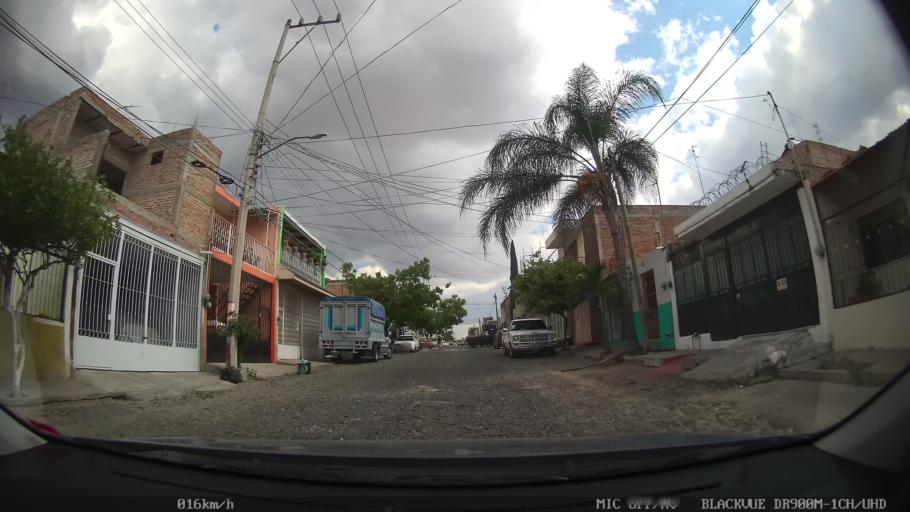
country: MX
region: Jalisco
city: Tlaquepaque
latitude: 20.6883
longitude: -103.2622
